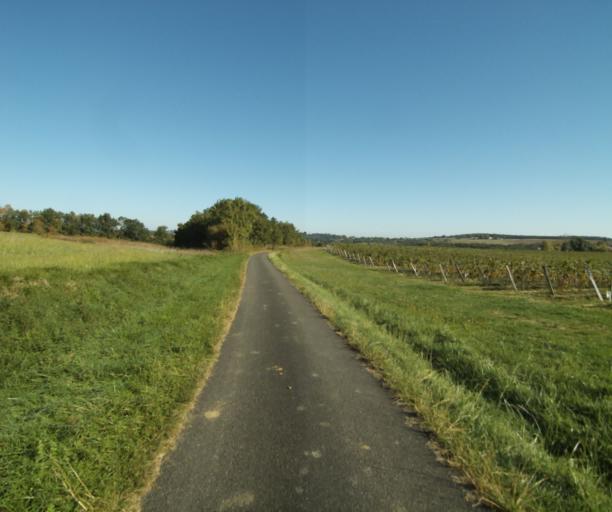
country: FR
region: Midi-Pyrenees
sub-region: Departement du Gers
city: Gondrin
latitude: 43.8227
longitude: 0.2396
